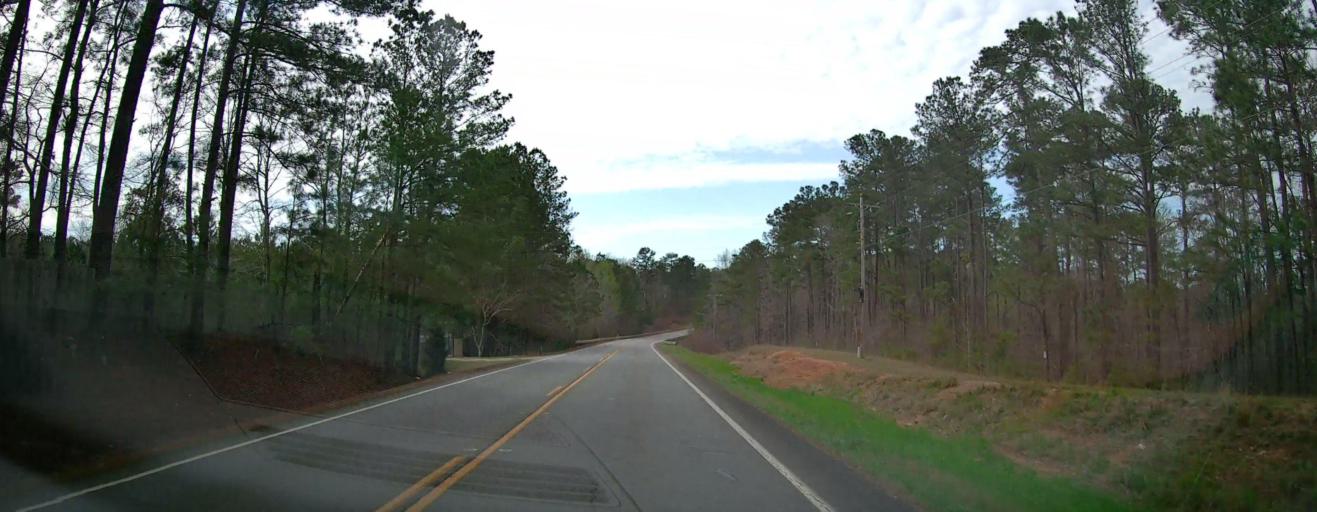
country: US
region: Georgia
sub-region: Jones County
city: Gray
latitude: 32.9876
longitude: -83.6813
